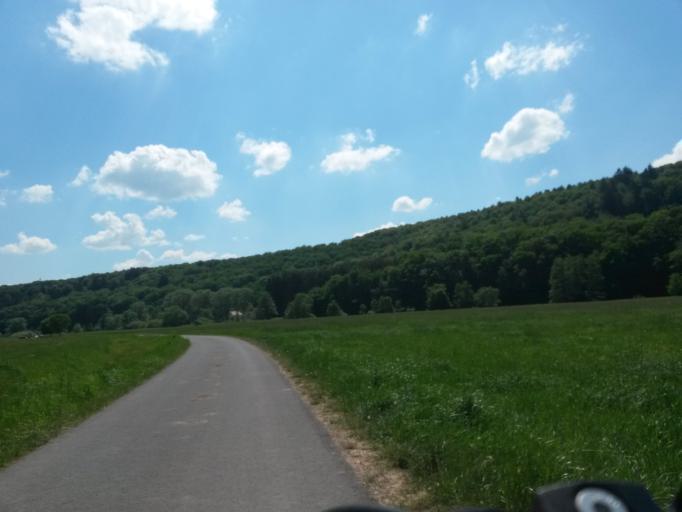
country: DE
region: Bavaria
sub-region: Regierungsbezirk Unterfranken
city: Bad Bocklet
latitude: 50.2450
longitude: 10.0621
